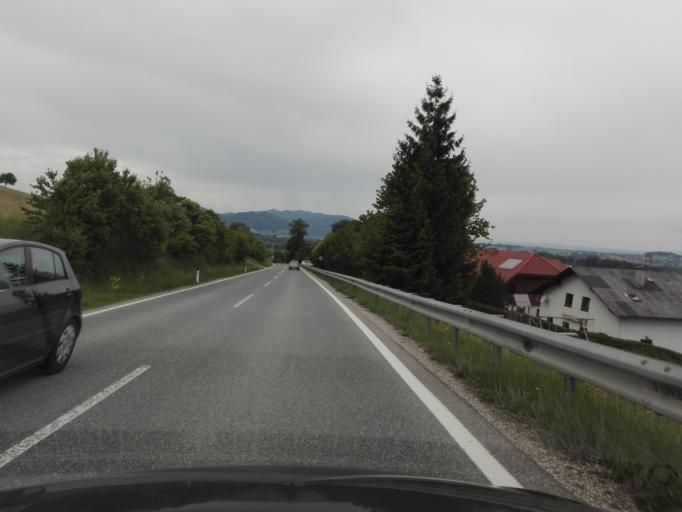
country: AT
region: Upper Austria
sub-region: Politischer Bezirk Gmunden
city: Gmunden
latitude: 47.9295
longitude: 13.8517
